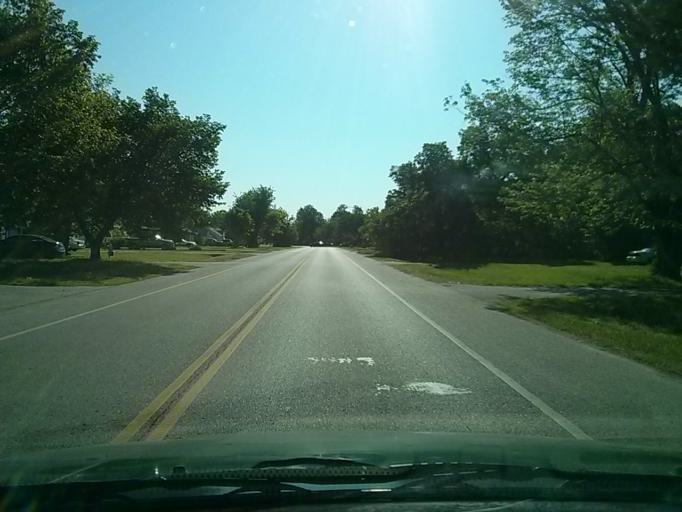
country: US
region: Oklahoma
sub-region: Tulsa County
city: Tulsa
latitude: 36.1925
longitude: -95.9915
